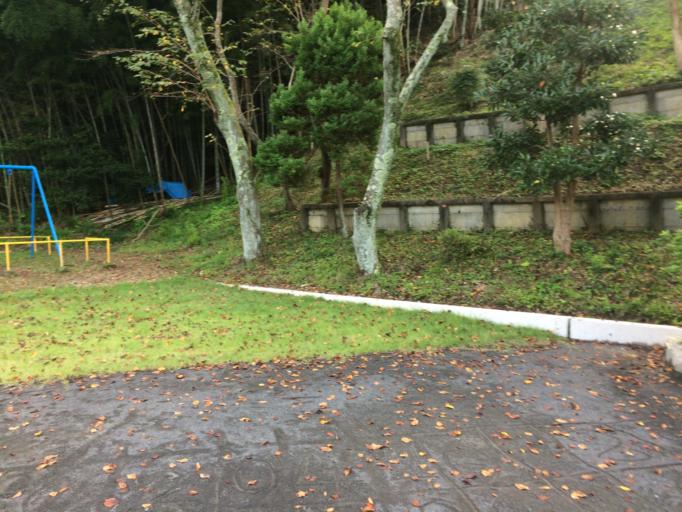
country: JP
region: Shizuoka
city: Shizuoka-shi
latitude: 34.9956
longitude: 138.4577
